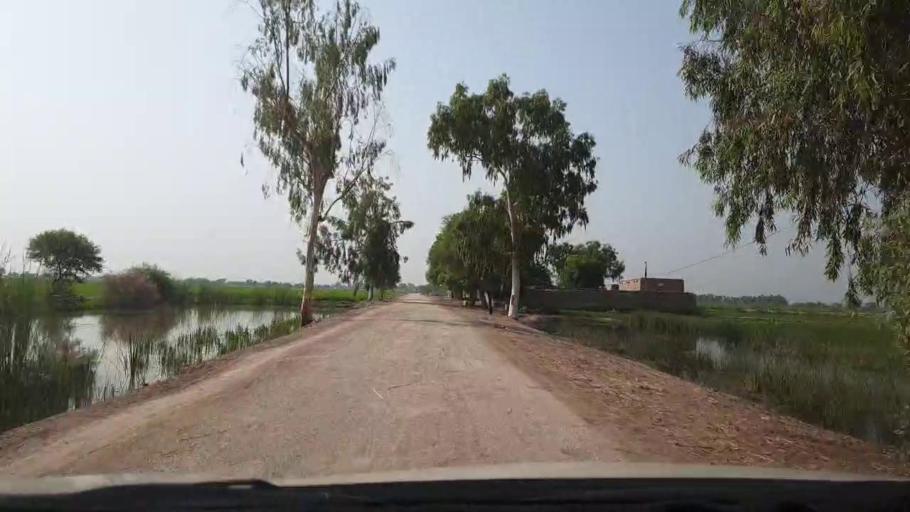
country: PK
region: Sindh
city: Goth Garelo
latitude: 27.4742
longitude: 68.0872
